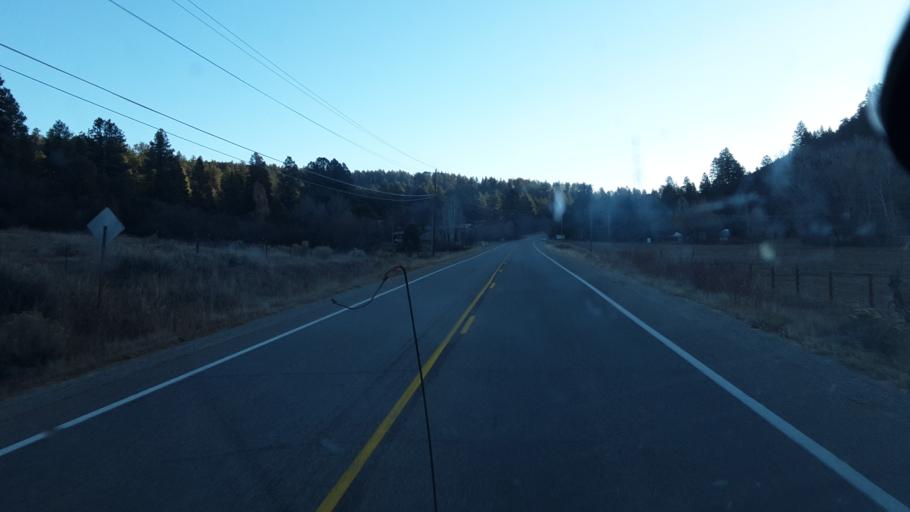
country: US
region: Colorado
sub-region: La Plata County
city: Durango
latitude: 37.3108
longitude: -107.8104
